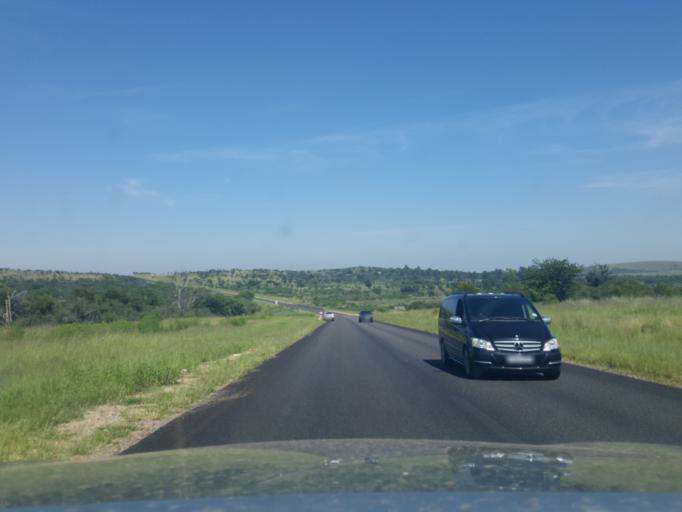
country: ZA
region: Gauteng
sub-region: City of Tshwane Metropolitan Municipality
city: Cullinan
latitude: -25.6811
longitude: 28.4930
